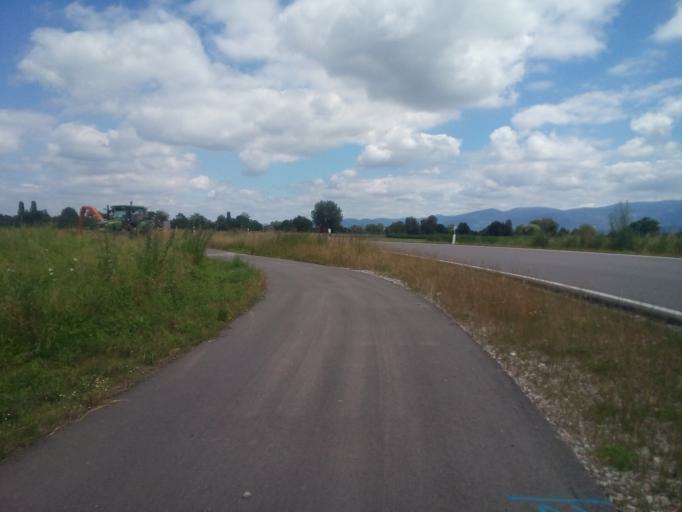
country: DE
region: Baden-Wuerttemberg
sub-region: Freiburg Region
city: Renchen
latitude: 48.6153
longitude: 7.9812
